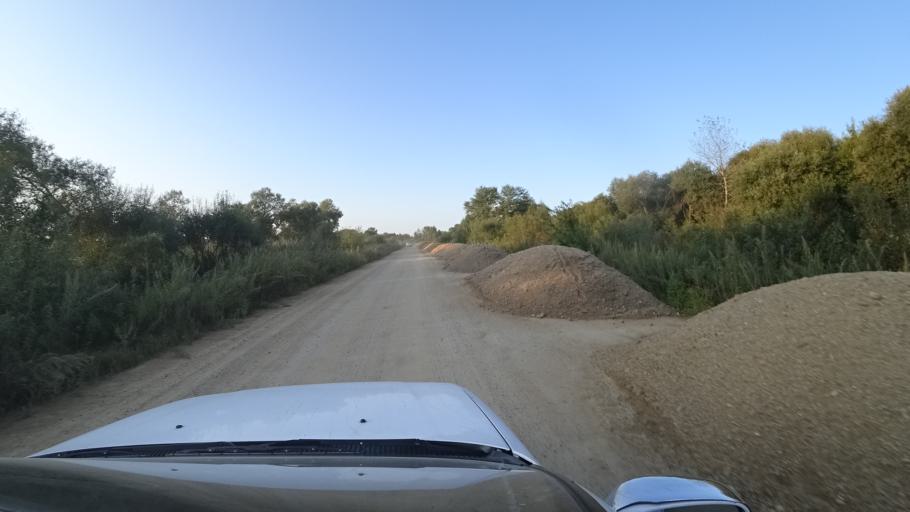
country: RU
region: Primorskiy
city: Dal'nerechensk
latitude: 45.9390
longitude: 133.7603
